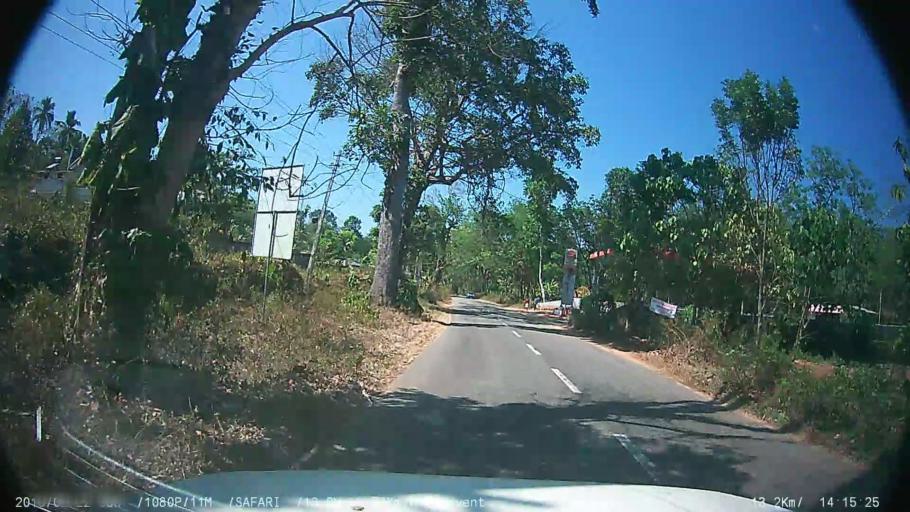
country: IN
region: Kerala
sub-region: Kottayam
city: Kottayam
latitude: 9.5495
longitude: 76.6836
